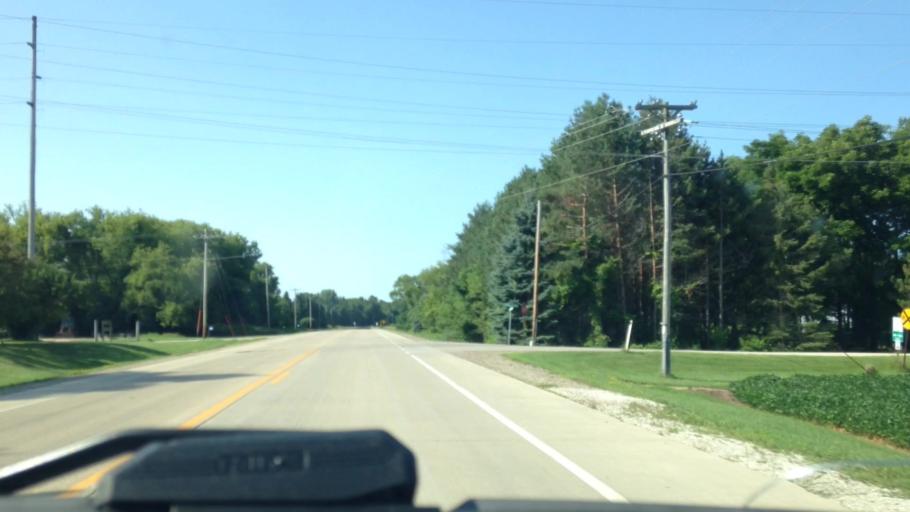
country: US
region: Wisconsin
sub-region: Dodge County
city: Mayville
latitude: 43.4799
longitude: -88.5542
